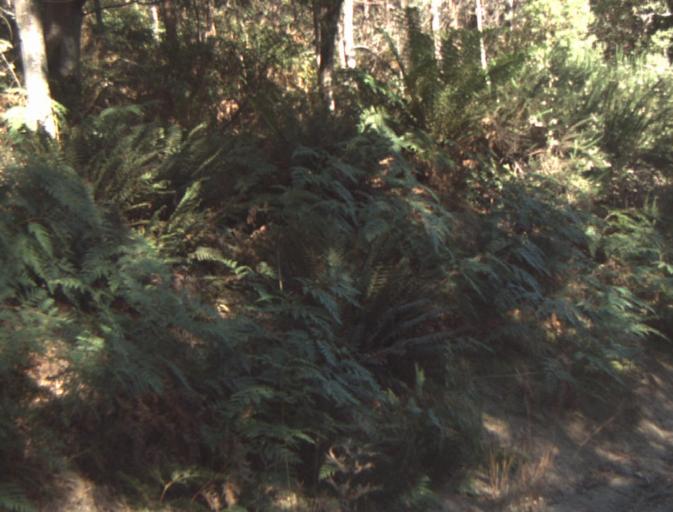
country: AU
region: Tasmania
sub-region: Dorset
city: Scottsdale
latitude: -41.2870
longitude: 147.3569
